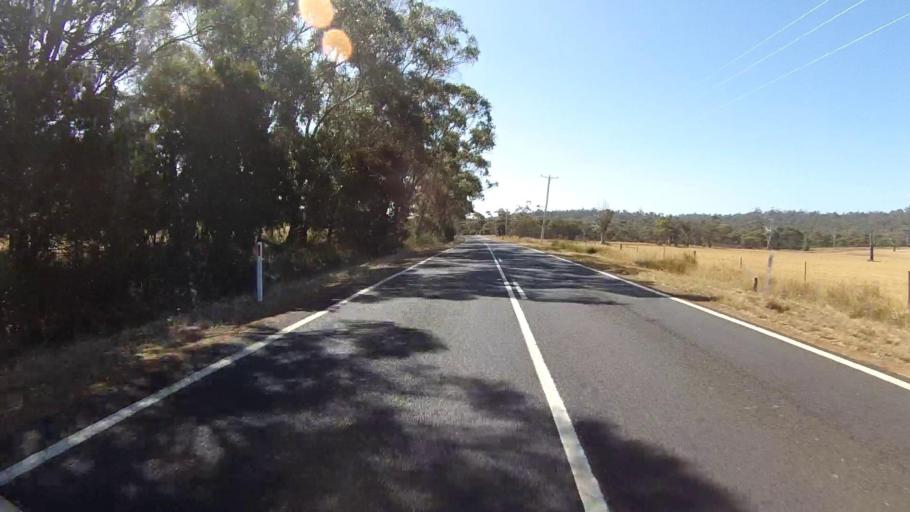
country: AU
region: Tasmania
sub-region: Sorell
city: Sorell
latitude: -42.4194
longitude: 147.9350
